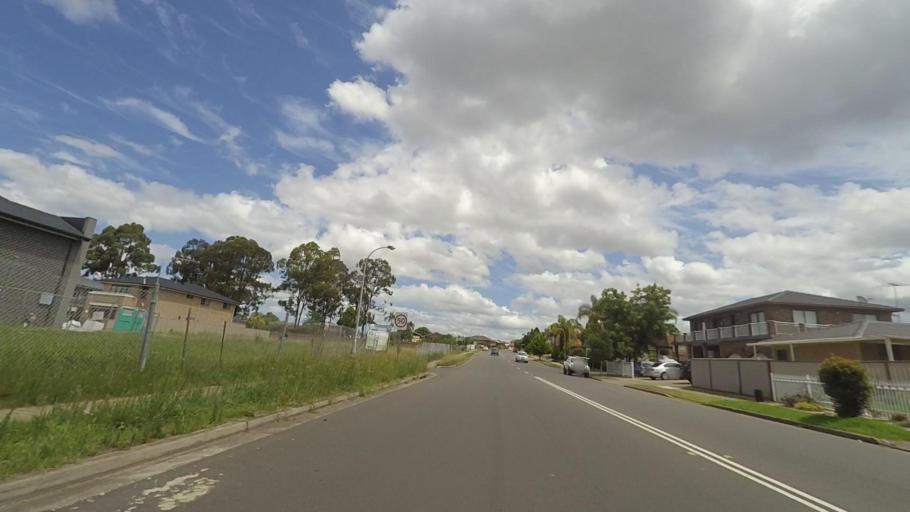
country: AU
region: New South Wales
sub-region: Fairfield
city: Cabramatta West
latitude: -33.8710
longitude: 150.9108
